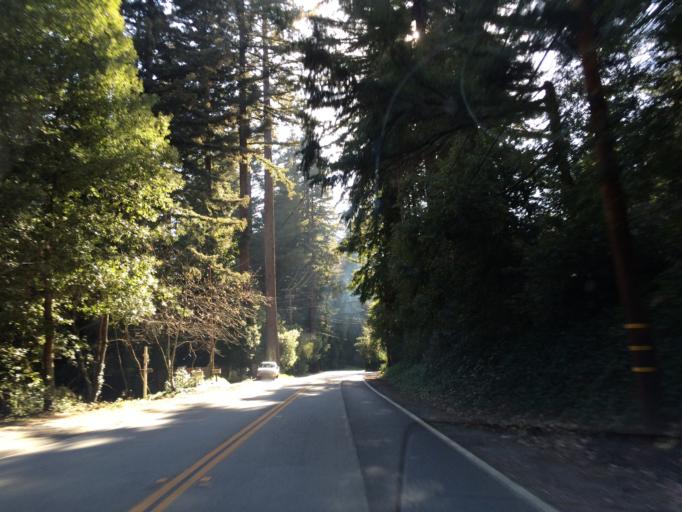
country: US
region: California
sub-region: Santa Cruz County
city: Boulder Creek
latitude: 37.1394
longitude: -122.1492
